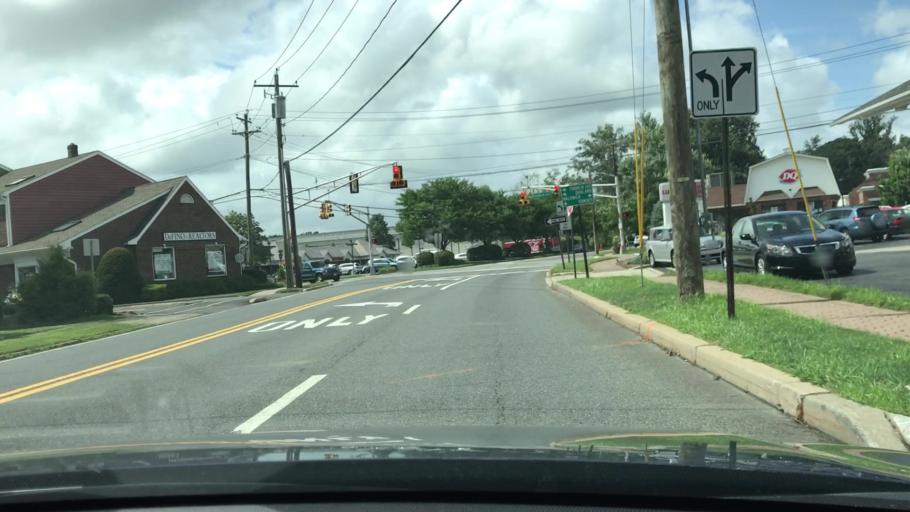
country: US
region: New Jersey
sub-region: Bergen County
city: Wyckoff
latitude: 41.0107
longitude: -74.1642
